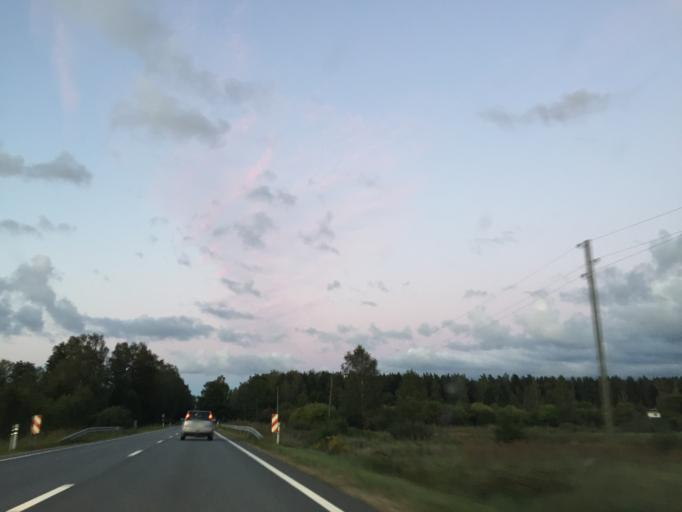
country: LV
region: Jurmala
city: Jurmala
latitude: 56.9088
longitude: 23.7769
